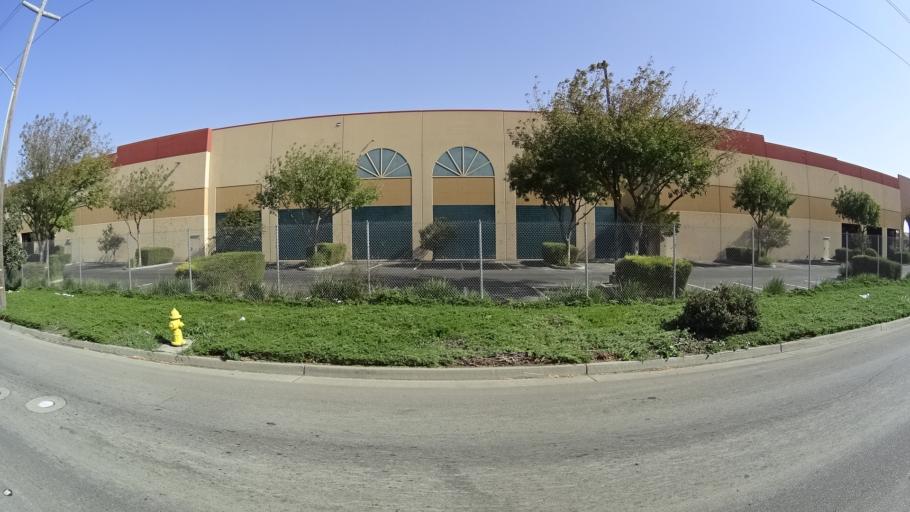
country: US
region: California
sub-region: Yolo County
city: Woodland
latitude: 38.6785
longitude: -121.7285
